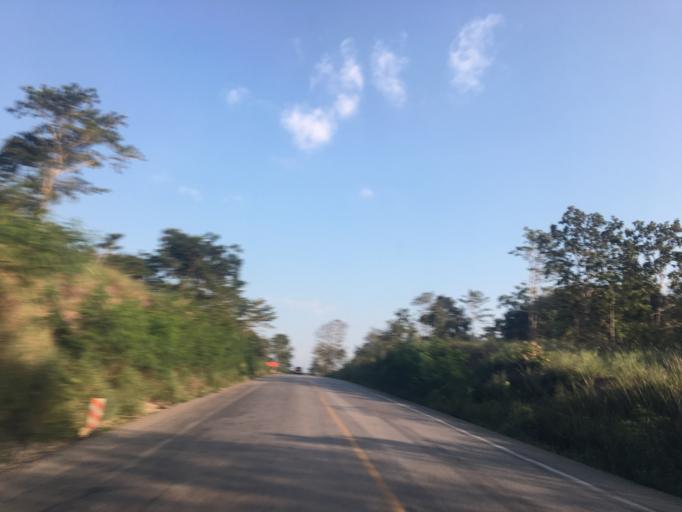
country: TH
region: Lampang
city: Ngao
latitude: 18.7038
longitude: 99.9961
